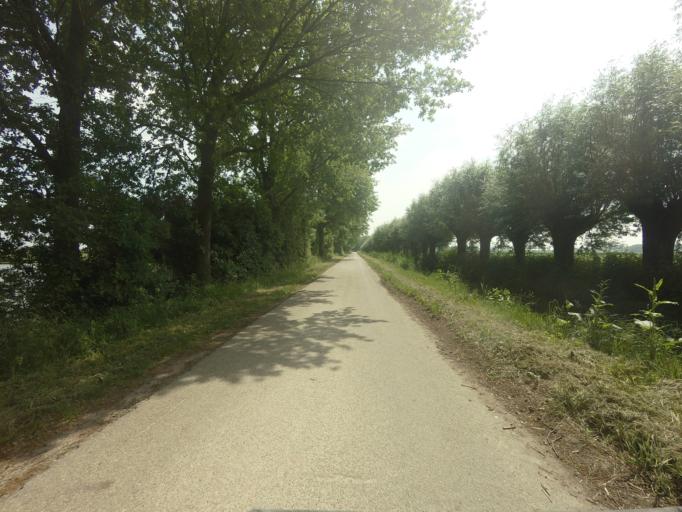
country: NL
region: Gelderland
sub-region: Gemeente Culemborg
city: Culemborg
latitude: 51.9908
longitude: 5.2362
